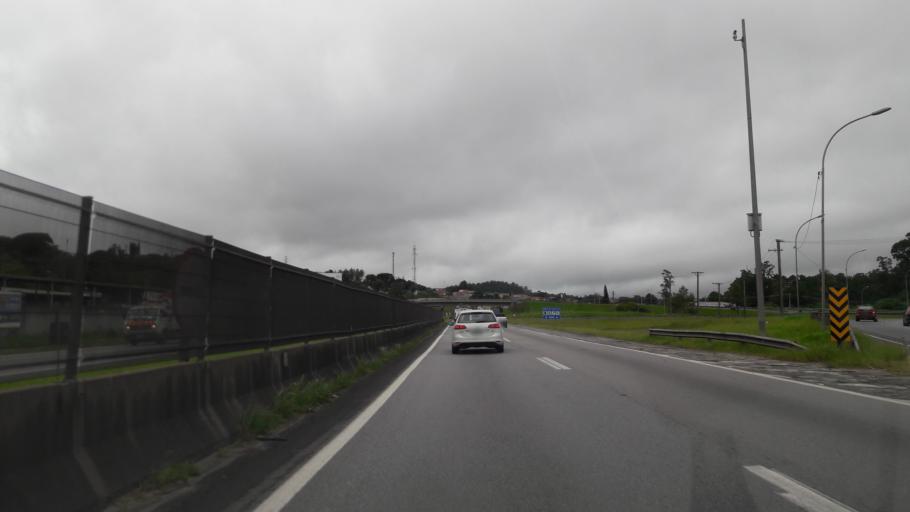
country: BR
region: Sao Paulo
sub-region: Embu
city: Embu
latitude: -23.6787
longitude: -46.8571
